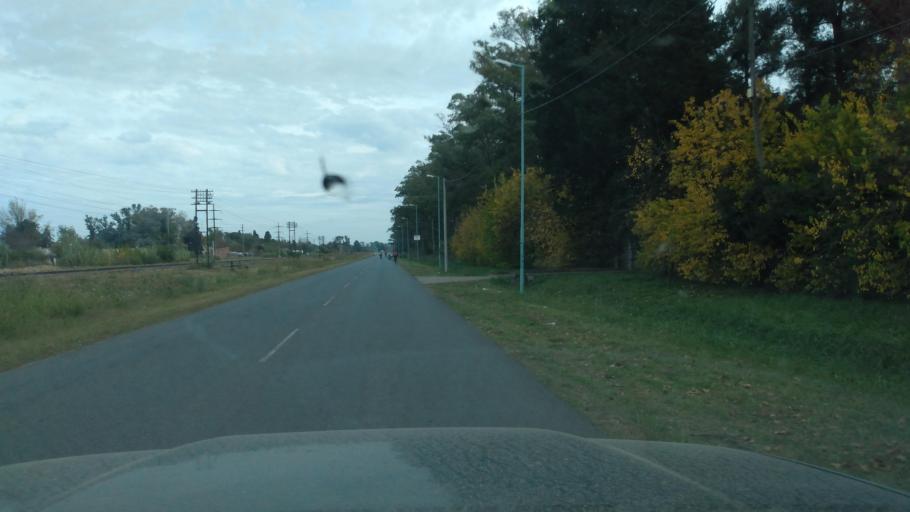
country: AR
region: Buenos Aires
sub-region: Partido de Lujan
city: Lujan
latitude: -34.5856
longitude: -59.1293
